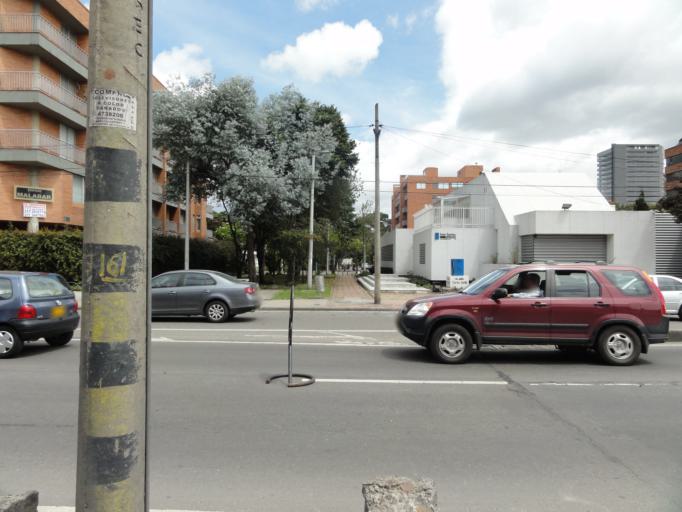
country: CO
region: Bogota D.C.
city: Barrio San Luis
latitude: 4.6993
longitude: -74.0538
